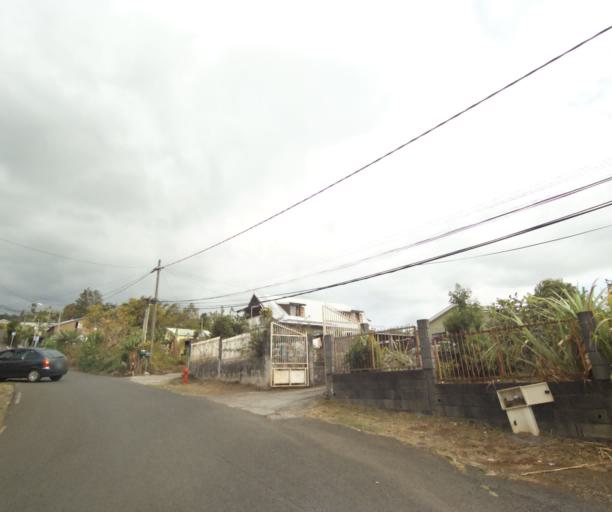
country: RE
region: Reunion
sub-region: Reunion
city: Saint-Paul
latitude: -21.0294
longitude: 55.3092
